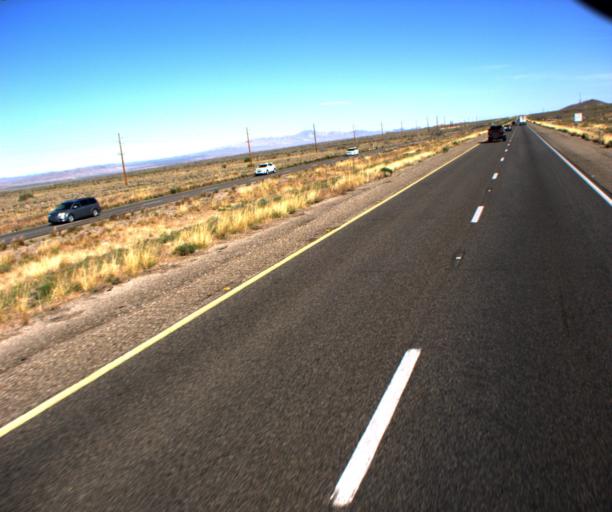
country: US
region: Arizona
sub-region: Mohave County
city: Golden Valley
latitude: 35.4016
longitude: -114.2626
